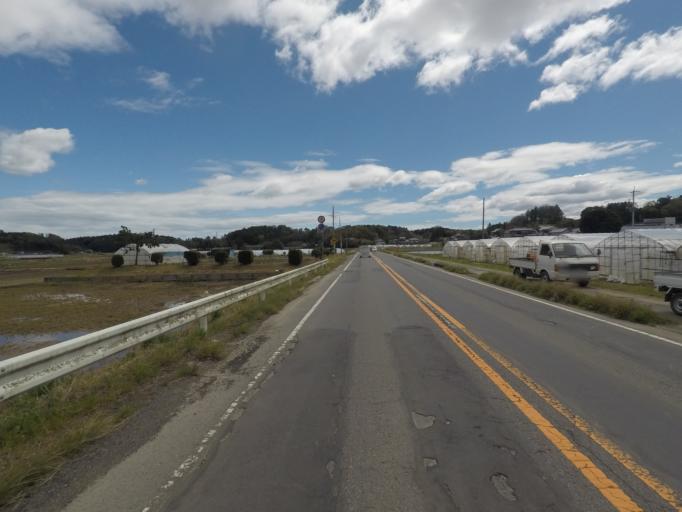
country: JP
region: Ibaraki
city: Itako
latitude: 36.0986
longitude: 140.5007
